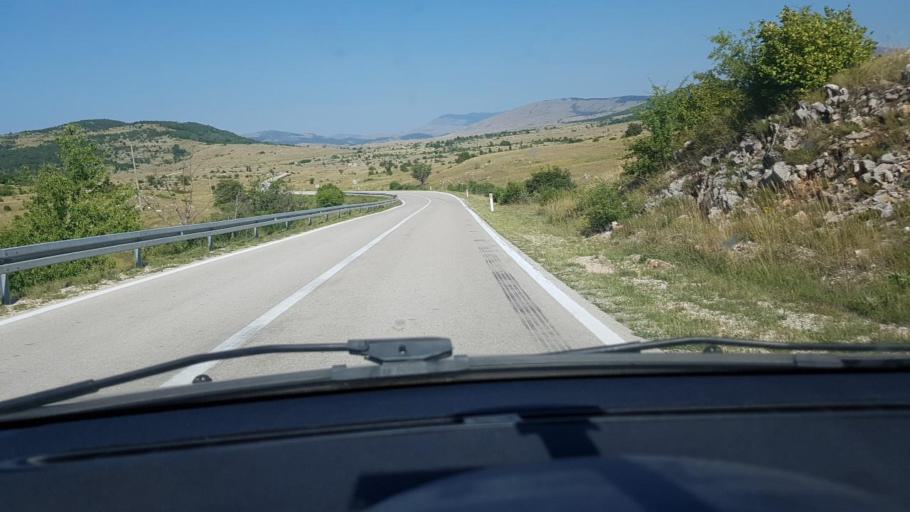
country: BA
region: Federation of Bosnia and Herzegovina
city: Bosansko Grahovo
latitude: 44.1301
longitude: 16.4930
